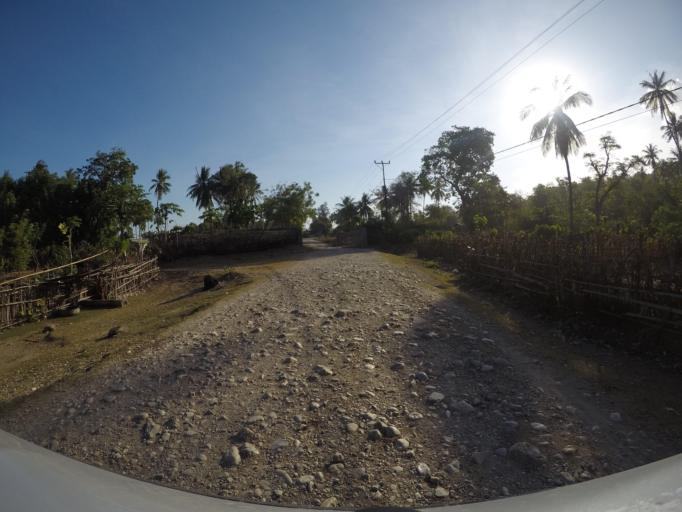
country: TL
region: Viqueque
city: Viqueque
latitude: -8.8028
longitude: 126.5840
